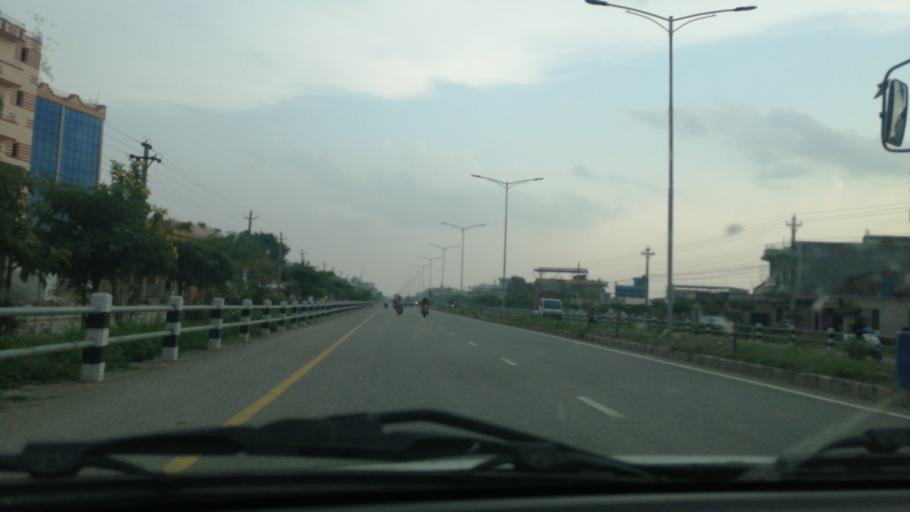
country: NP
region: Western Region
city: Butwal
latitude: 27.6372
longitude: 83.4717
